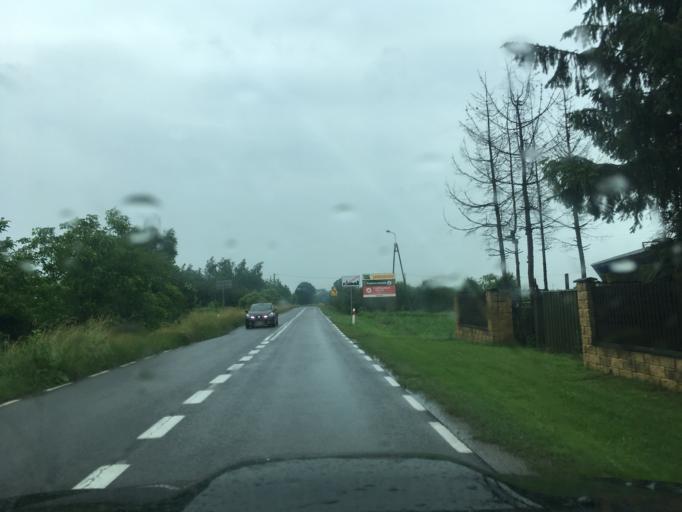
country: PL
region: Masovian Voivodeship
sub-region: Powiat piaseczynski
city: Gora Kalwaria
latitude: 51.9819
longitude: 21.2700
